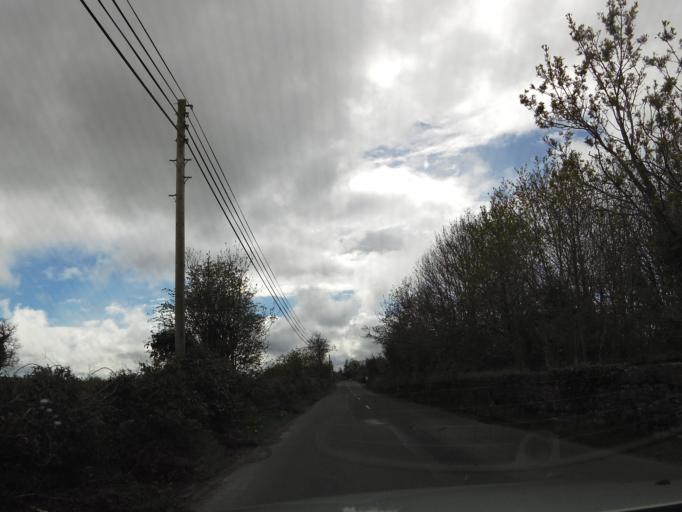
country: IE
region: Connaught
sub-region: Maigh Eo
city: Ballinrobe
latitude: 53.5606
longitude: -9.2446
